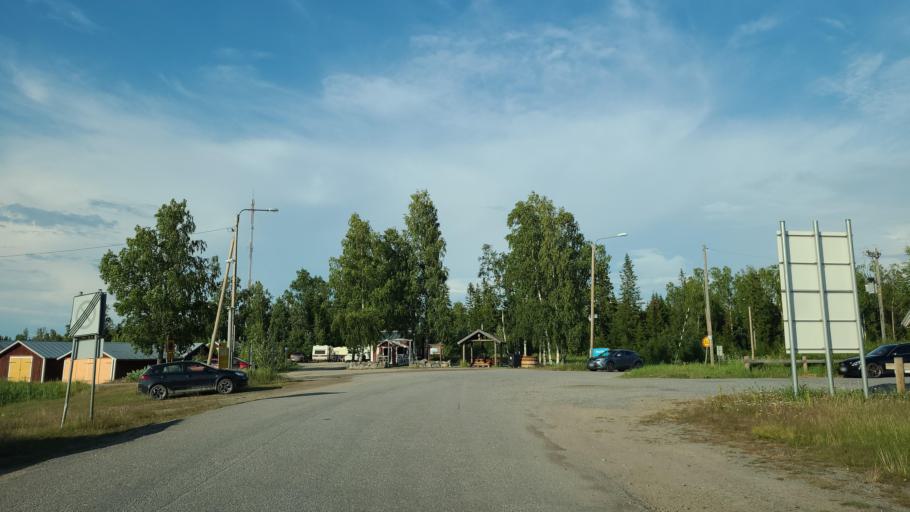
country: FI
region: Ostrobothnia
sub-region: Vaasa
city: Replot
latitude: 63.3600
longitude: 21.3006
